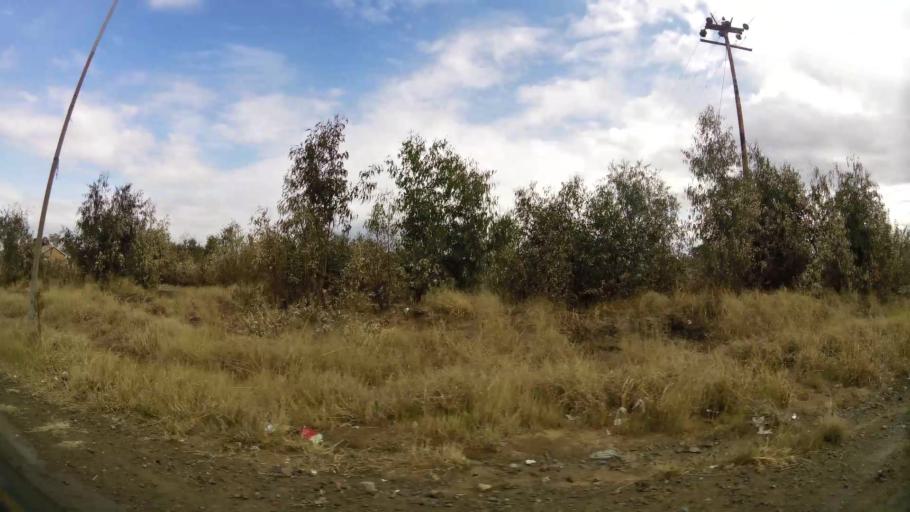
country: ZA
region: Orange Free State
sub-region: Fezile Dabi District Municipality
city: Kroonstad
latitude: -27.6446
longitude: 27.2221
